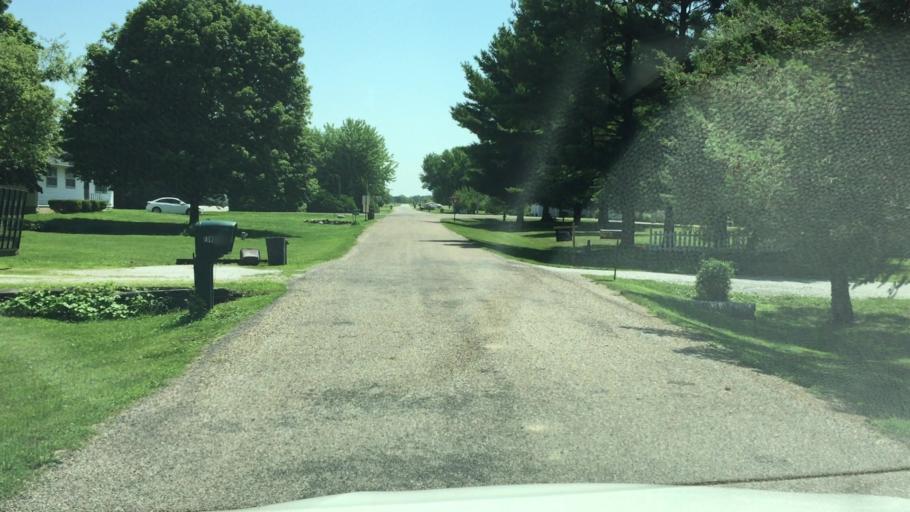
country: US
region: Illinois
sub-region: Hancock County
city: Nauvoo
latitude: 40.5326
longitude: -91.3715
